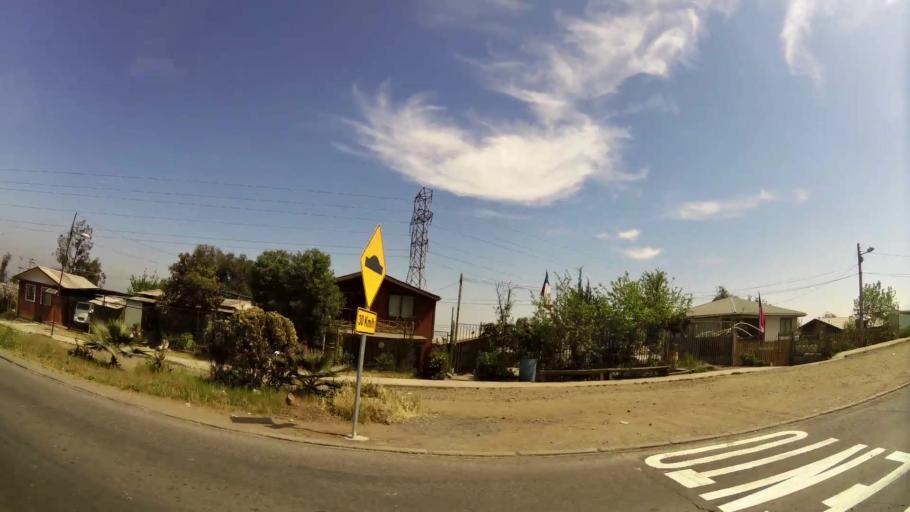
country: CL
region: Santiago Metropolitan
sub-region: Provincia de Santiago
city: Villa Presidente Frei, Nunoa, Santiago, Chile
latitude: -33.4768
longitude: -70.5251
